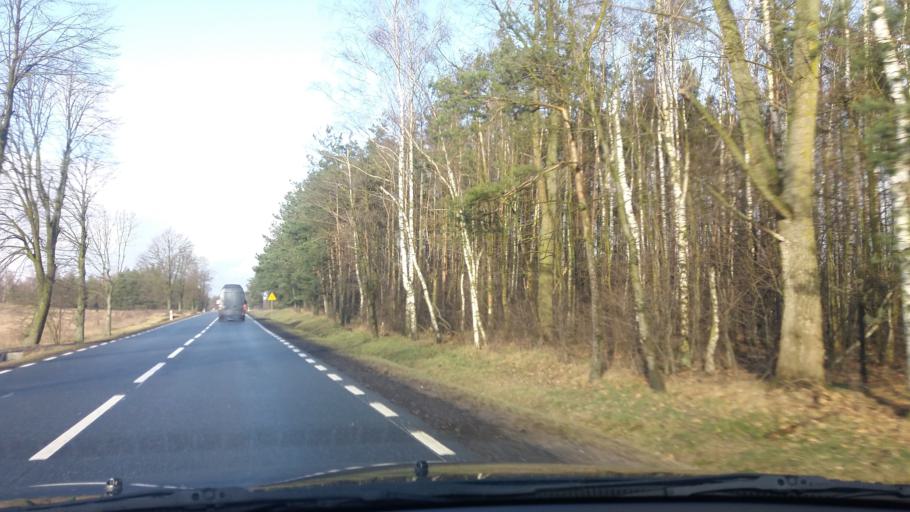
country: PL
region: Masovian Voivodeship
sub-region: Powiat przasnyski
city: Chorzele
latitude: 53.2700
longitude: 20.8989
